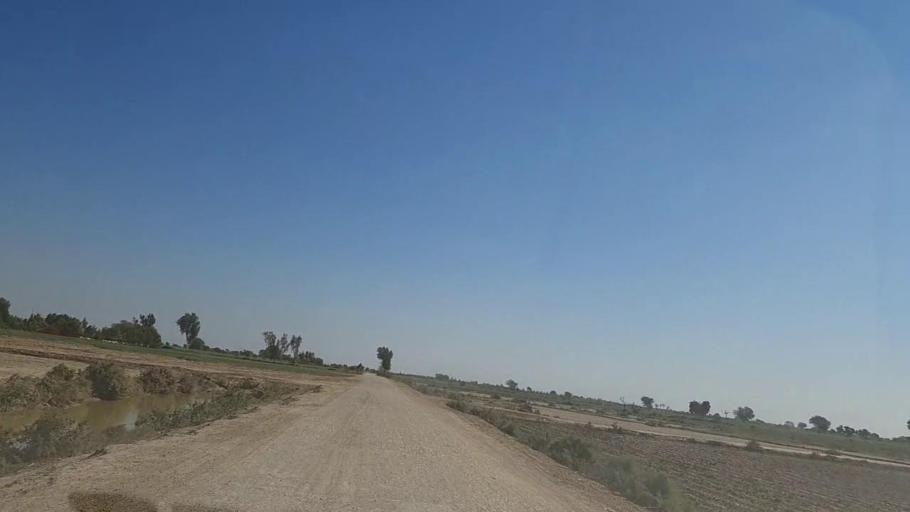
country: PK
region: Sindh
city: Digri
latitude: 25.1128
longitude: 69.1158
